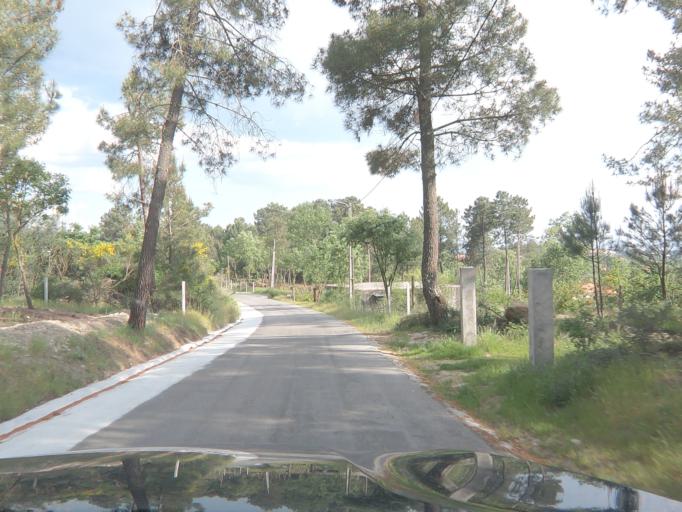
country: PT
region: Vila Real
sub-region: Vila Real
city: Vila Real
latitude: 41.3523
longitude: -7.7256
